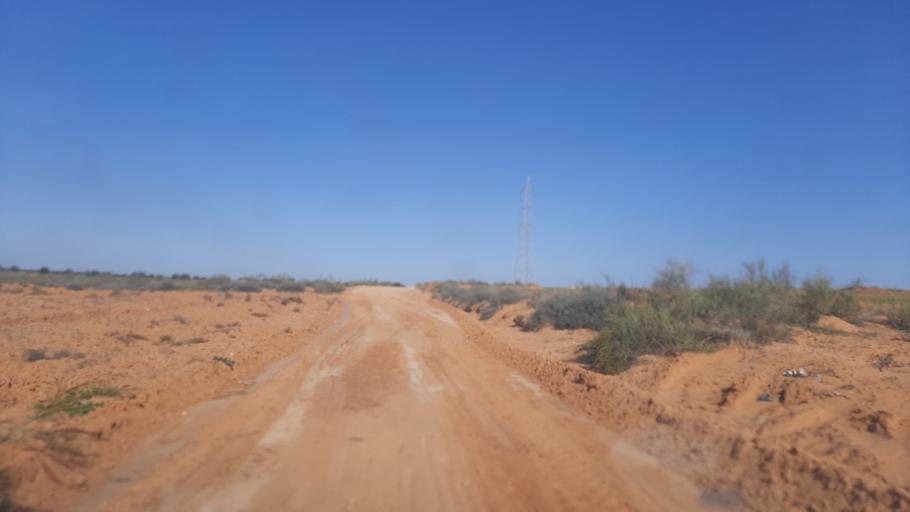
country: TN
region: Madanin
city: Medenine
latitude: 33.2776
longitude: 10.7739
